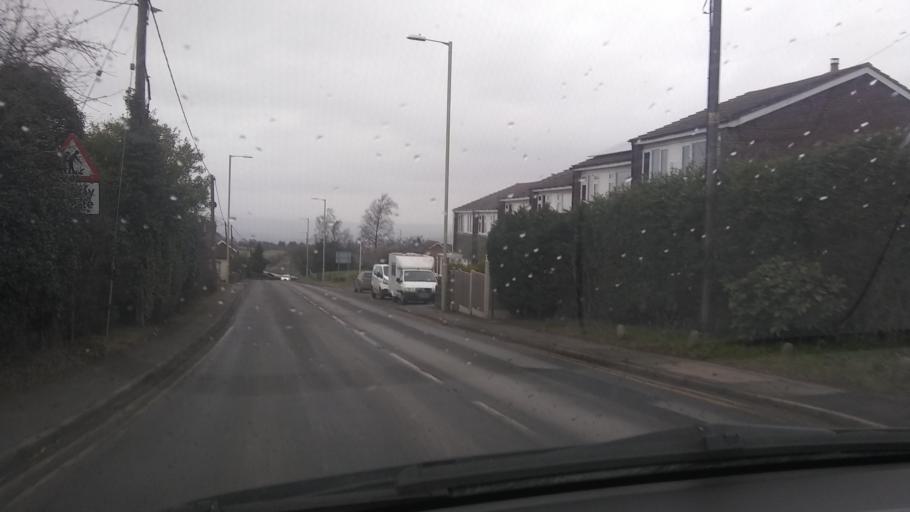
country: GB
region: England
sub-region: Worcestershire
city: Tenbury Wells
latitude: 52.3746
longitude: -2.6003
